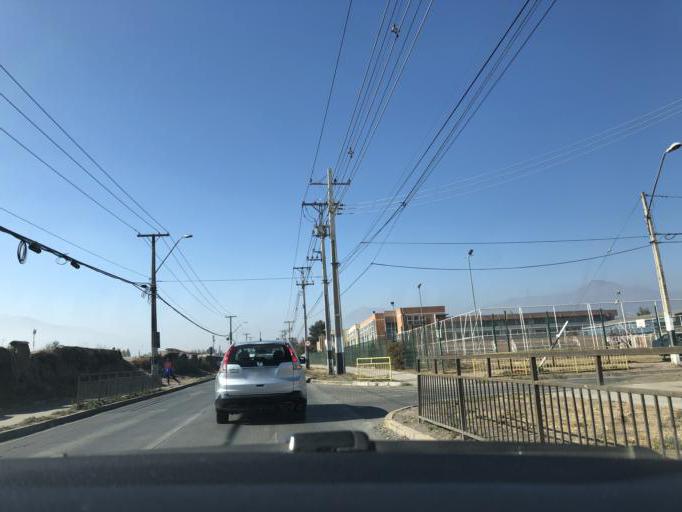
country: CL
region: Santiago Metropolitan
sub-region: Provincia de Santiago
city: La Pintana
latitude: -33.6172
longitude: -70.6154
